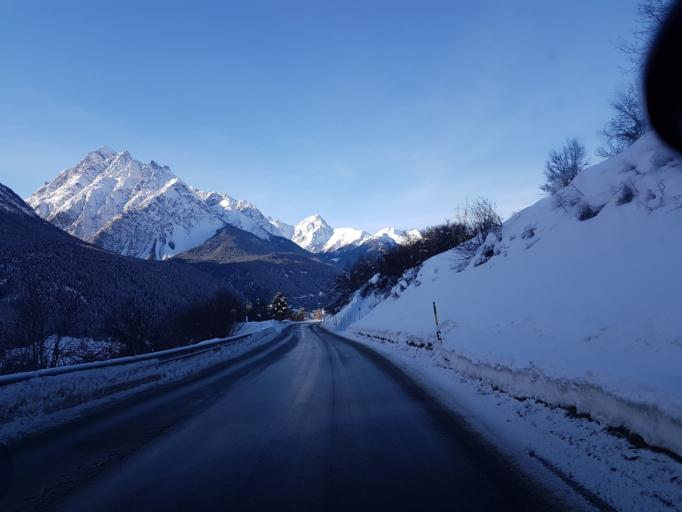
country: CH
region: Grisons
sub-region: Inn District
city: Scuol
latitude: 46.8087
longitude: 10.3209
